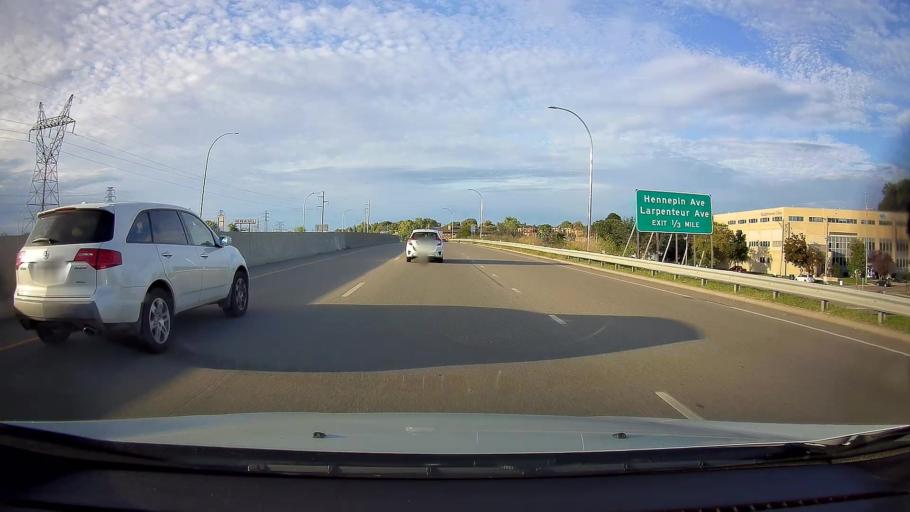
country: US
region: Minnesota
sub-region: Ramsey County
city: Lauderdale
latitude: 44.9856
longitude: -93.2032
